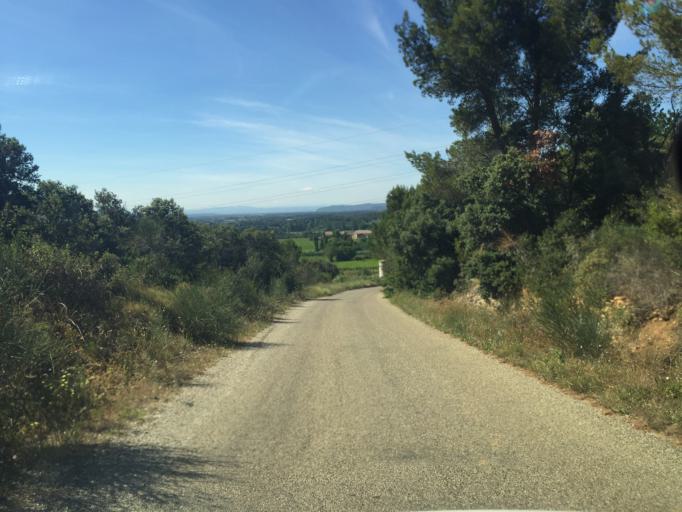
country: FR
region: Provence-Alpes-Cote d'Azur
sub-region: Departement du Vaucluse
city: Chateauneuf-du-Pape
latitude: 44.0870
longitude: 4.8047
